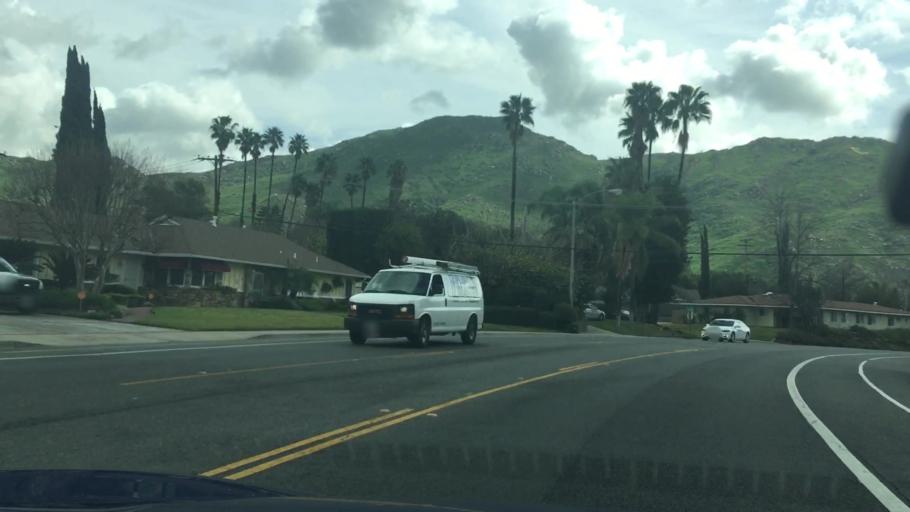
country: US
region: California
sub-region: Riverside County
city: Highgrove
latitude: 33.9792
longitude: -117.3175
